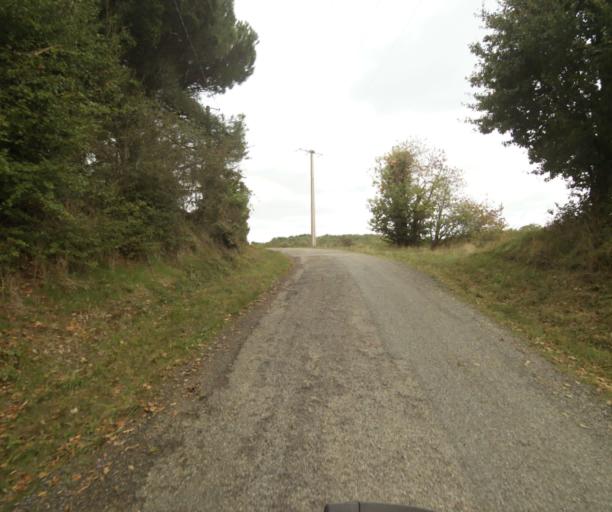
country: FR
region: Midi-Pyrenees
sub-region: Departement du Tarn-et-Garonne
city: Beaumont-de-Lomagne
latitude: 43.8480
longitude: 1.0743
